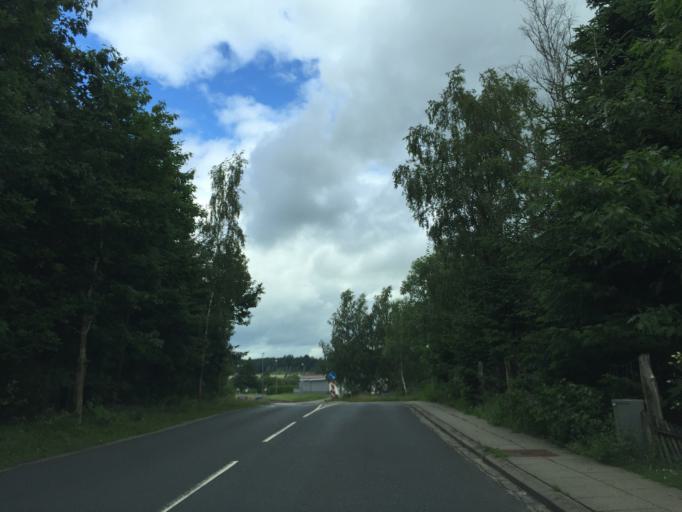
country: DK
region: Central Jutland
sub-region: Silkeborg Kommune
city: Svejbaek
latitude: 56.1802
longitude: 9.6442
